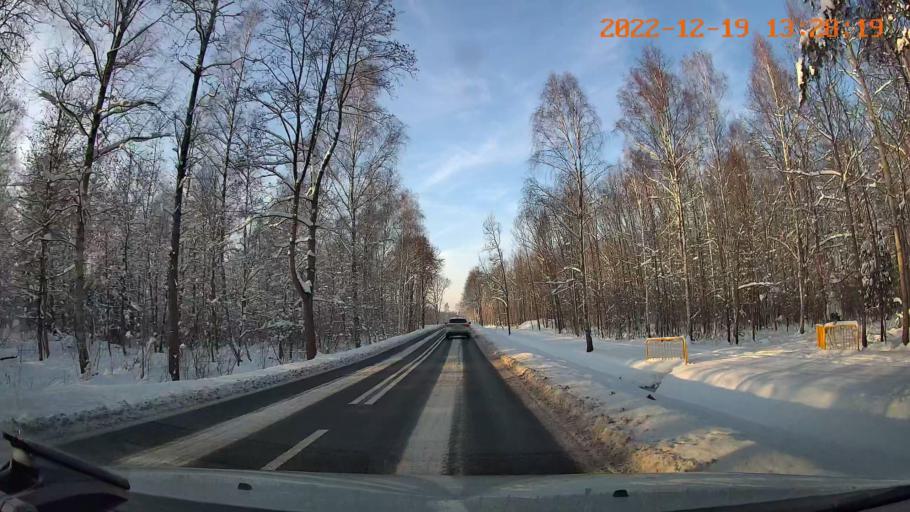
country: PL
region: Silesian Voivodeship
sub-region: Powiat bierunsko-ledzinski
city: Ledziny
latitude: 50.1113
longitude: 19.1293
